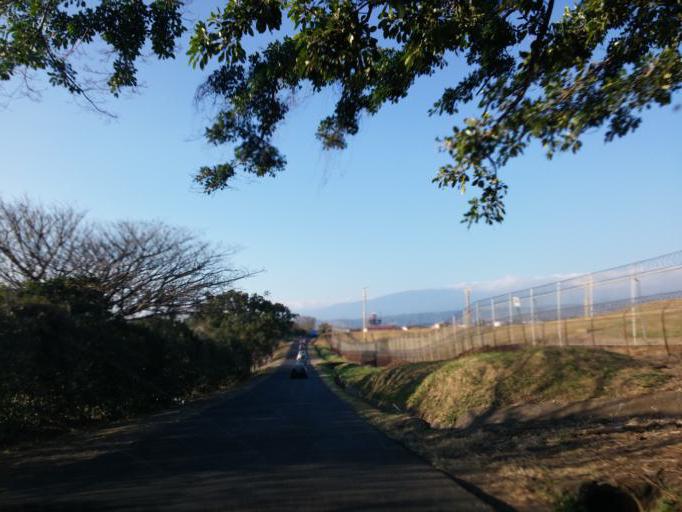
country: CR
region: Alajuela
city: Alajuela
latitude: 9.9872
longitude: -84.2233
